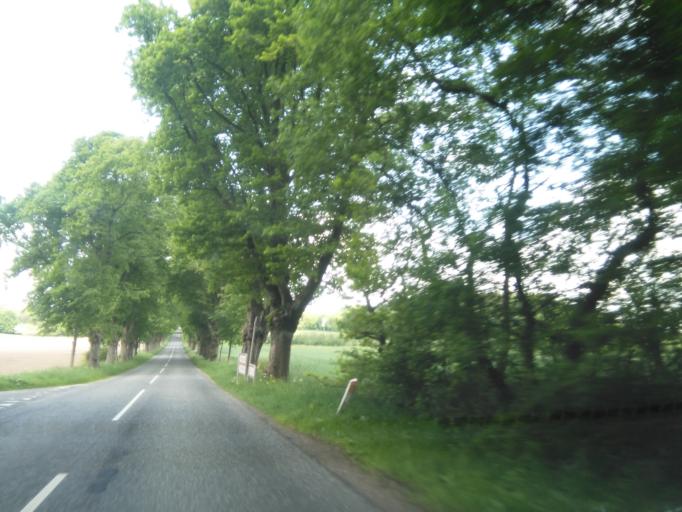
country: DK
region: Central Jutland
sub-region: Favrskov Kommune
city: Hammel
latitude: 56.2578
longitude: 9.9046
